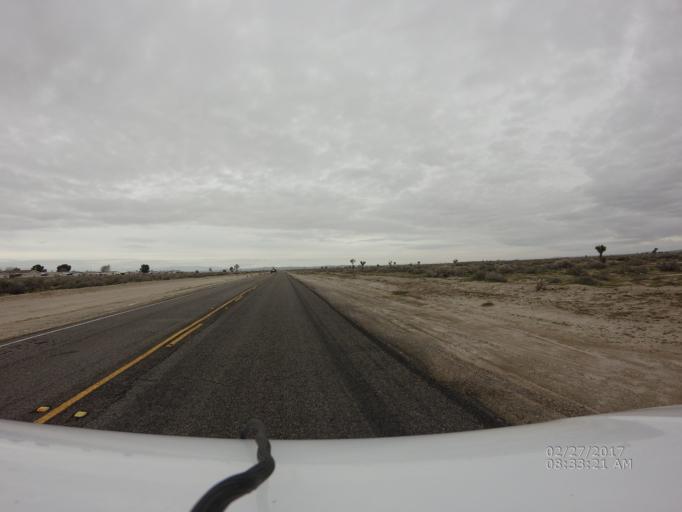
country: US
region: California
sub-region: Los Angeles County
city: Lancaster
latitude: 34.7053
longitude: -118.0594
